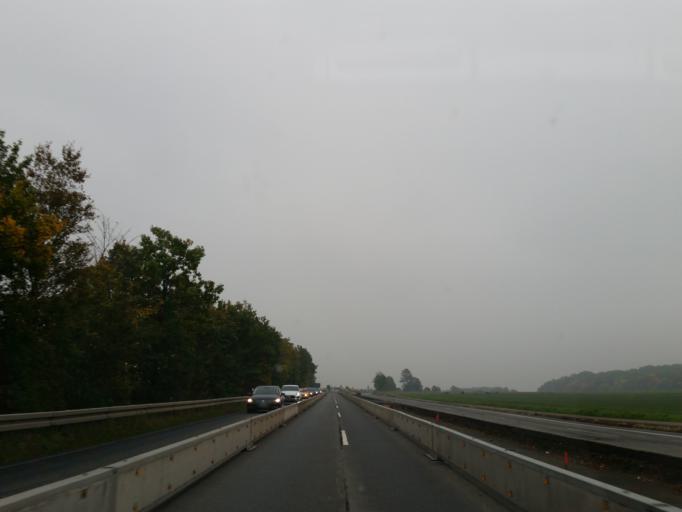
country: DE
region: Lower Saxony
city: Vienenburg
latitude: 51.9700
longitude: 10.5679
